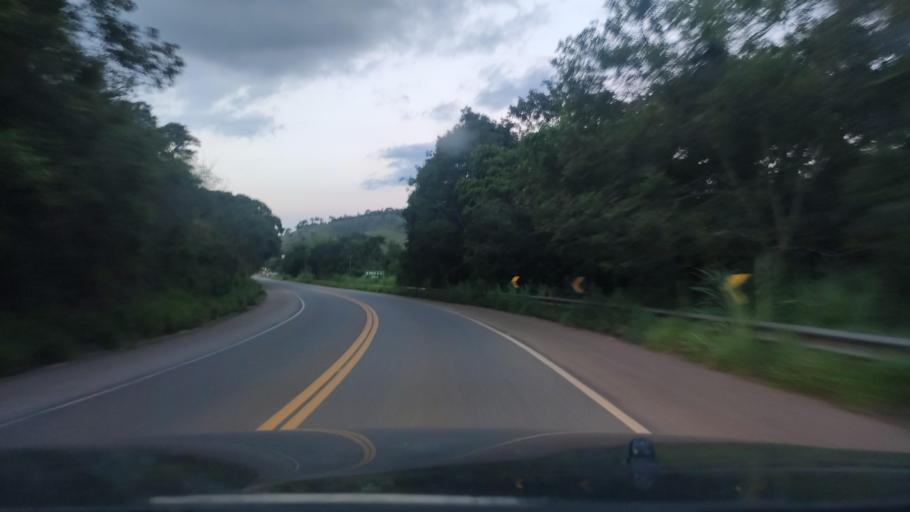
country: BR
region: Sao Paulo
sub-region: Campos Do Jordao
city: Campos do Jordao
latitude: -22.7906
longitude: -45.7436
